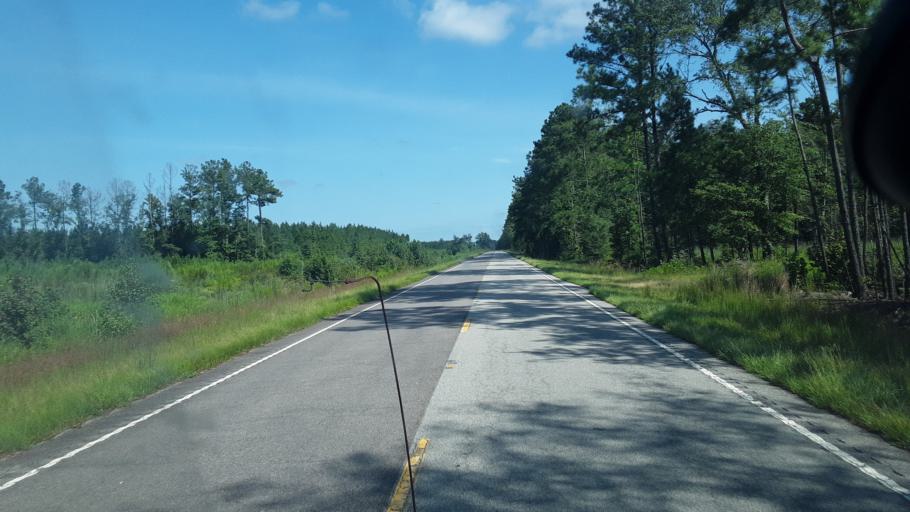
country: US
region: South Carolina
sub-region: Hampton County
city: Varnville
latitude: 32.8082
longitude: -81.0519
